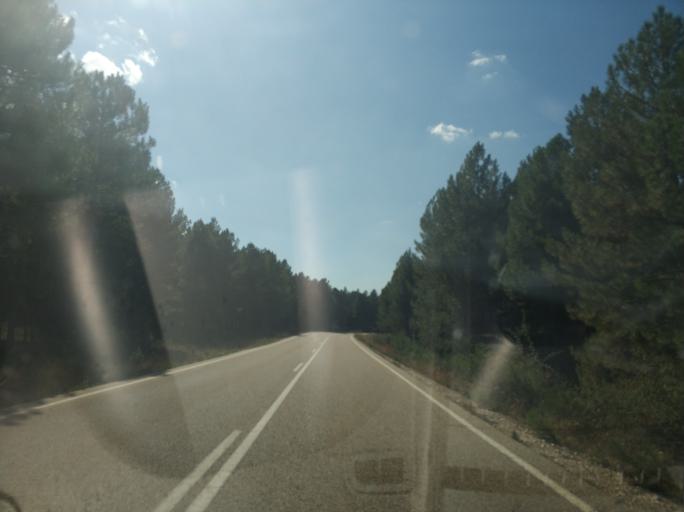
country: ES
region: Castille and Leon
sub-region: Provincia de Soria
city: Herrera de Soria
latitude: 41.7617
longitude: -3.0339
